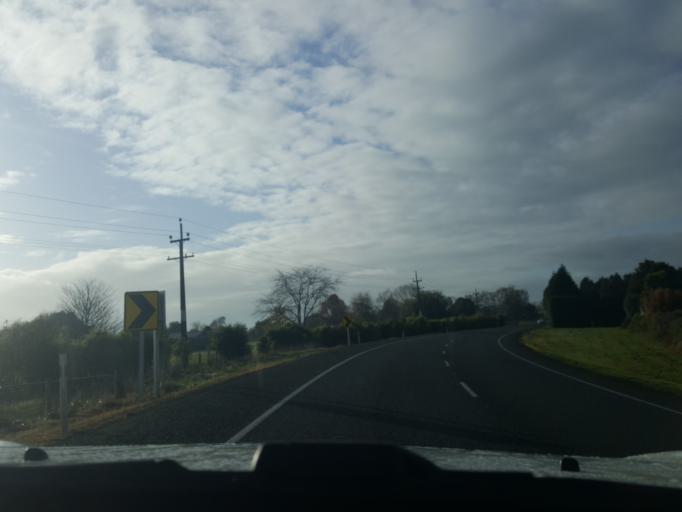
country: NZ
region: Waikato
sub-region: Hamilton City
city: Hamilton
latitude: -37.7734
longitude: 175.3679
